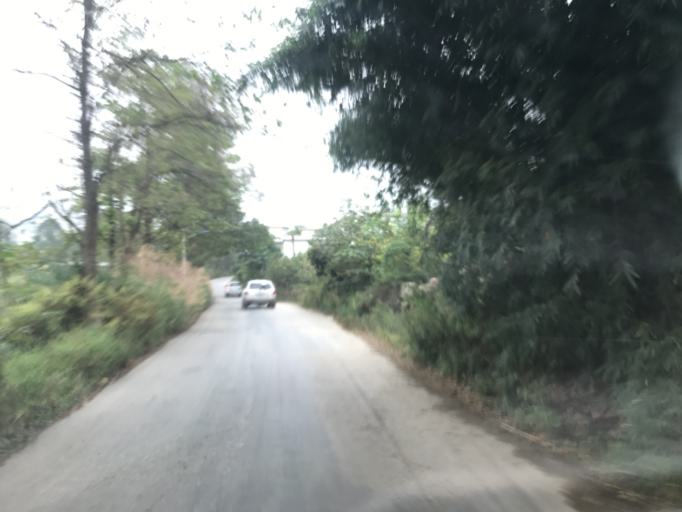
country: CN
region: Guizhou Sheng
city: Guiyang
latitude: 26.7031
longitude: 106.8740
